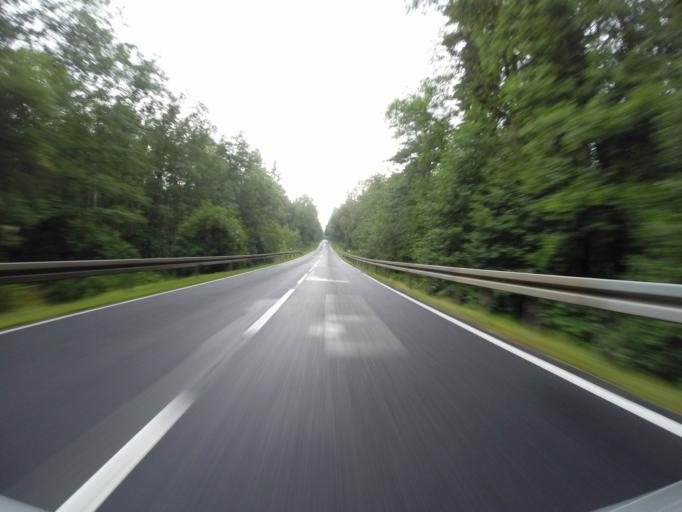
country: DE
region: Thuringia
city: Schleifreisen
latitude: 50.9026
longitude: 11.8128
